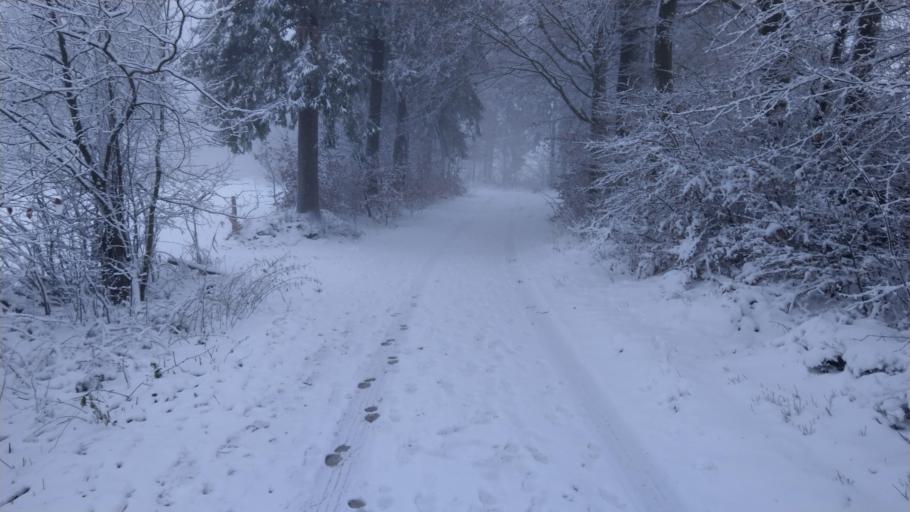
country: DE
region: North Rhine-Westphalia
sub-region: Regierungsbezirk Koln
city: Monschau
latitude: 50.5713
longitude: 6.2054
